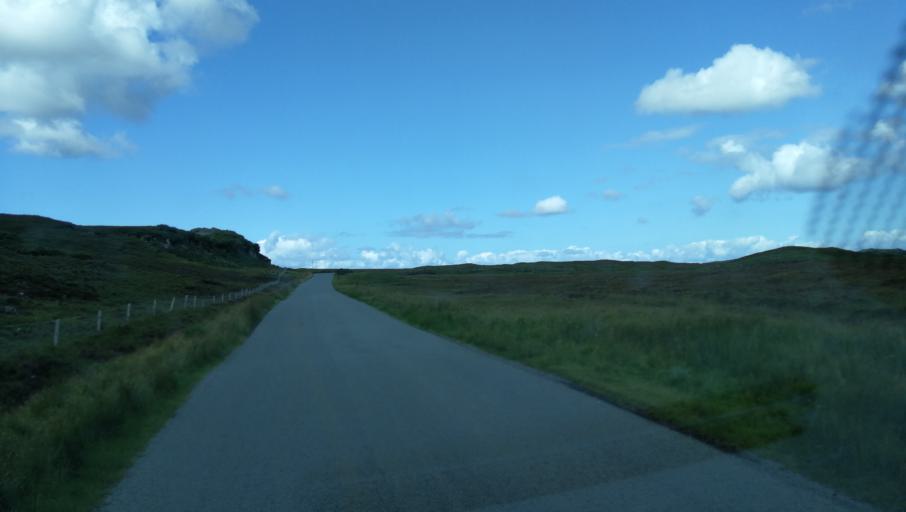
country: GB
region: Scotland
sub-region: Highland
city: Isle of Skye
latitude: 57.4229
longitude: -6.5932
